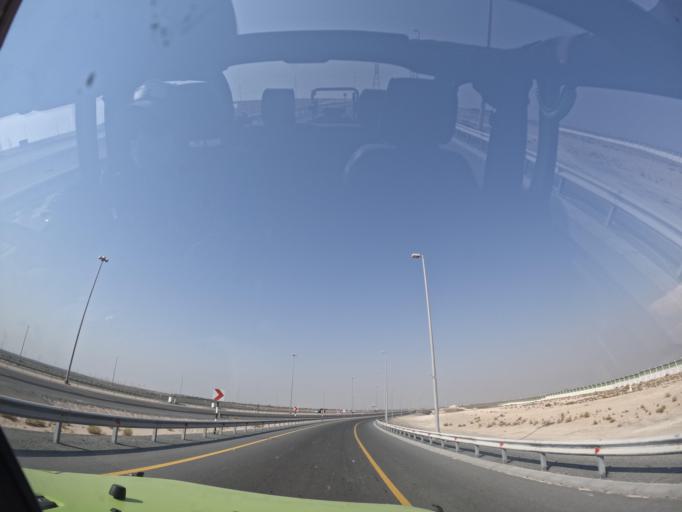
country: AE
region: Abu Dhabi
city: Abu Dhabi
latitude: 24.6178
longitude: 54.7671
